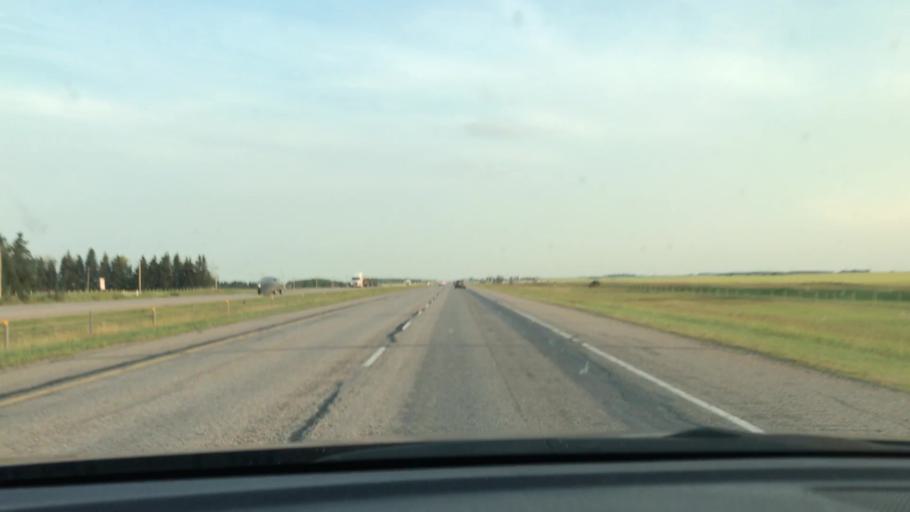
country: CA
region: Alberta
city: Olds
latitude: 51.8597
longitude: -114.0256
